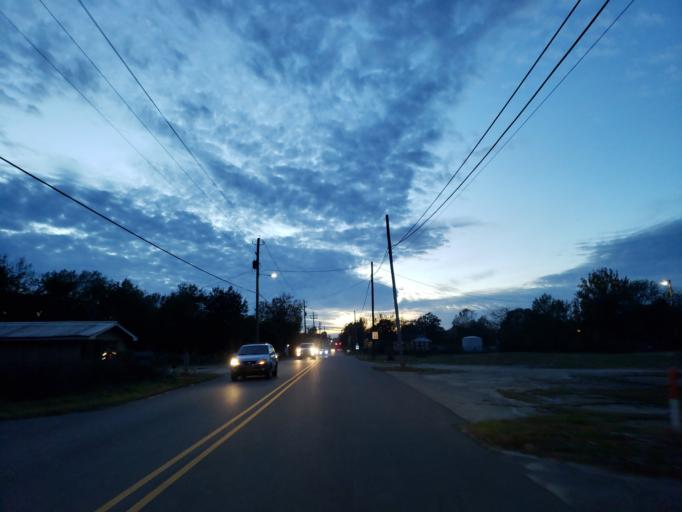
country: US
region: Mississippi
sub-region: Forrest County
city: Hattiesburg
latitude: 31.3251
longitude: -89.2759
